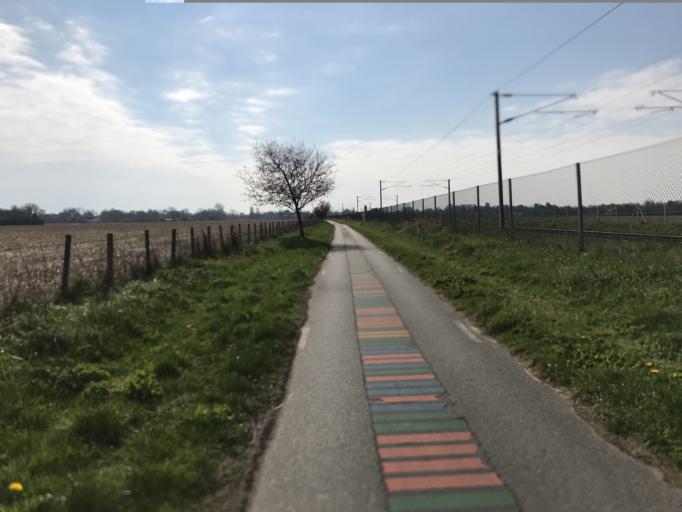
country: GB
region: England
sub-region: Cambridgeshire
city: Cambridge
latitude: 52.1636
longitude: 0.1329
